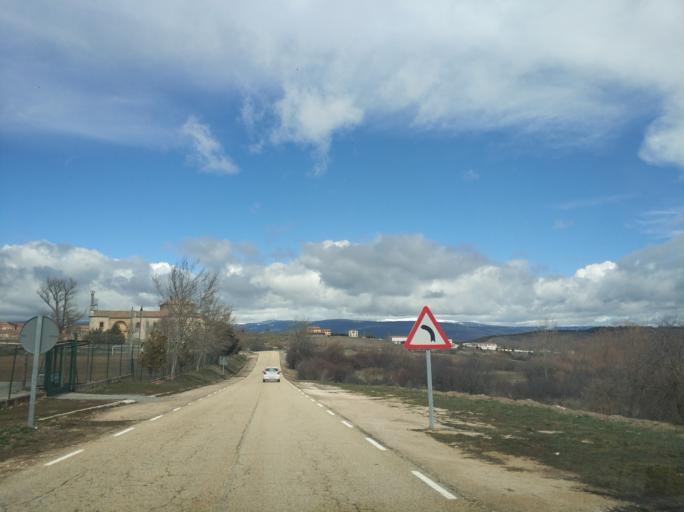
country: ES
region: Castille and Leon
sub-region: Provincia de Soria
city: Abejar
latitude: 41.8022
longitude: -2.7812
